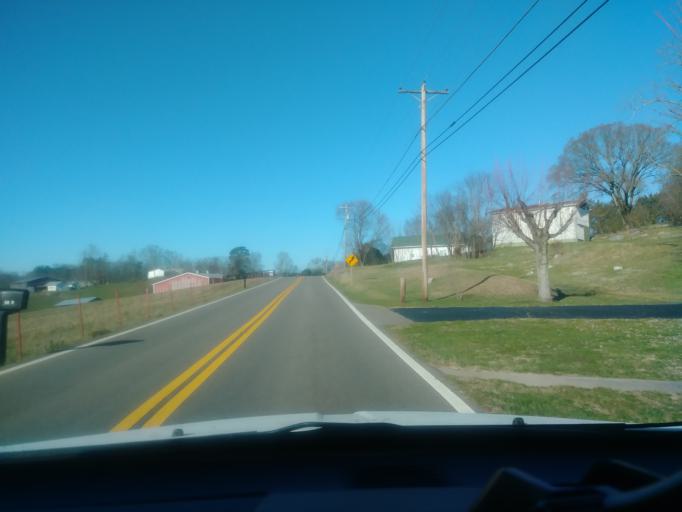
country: US
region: Tennessee
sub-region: Greene County
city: Mosheim
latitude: 36.1159
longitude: -82.9619
